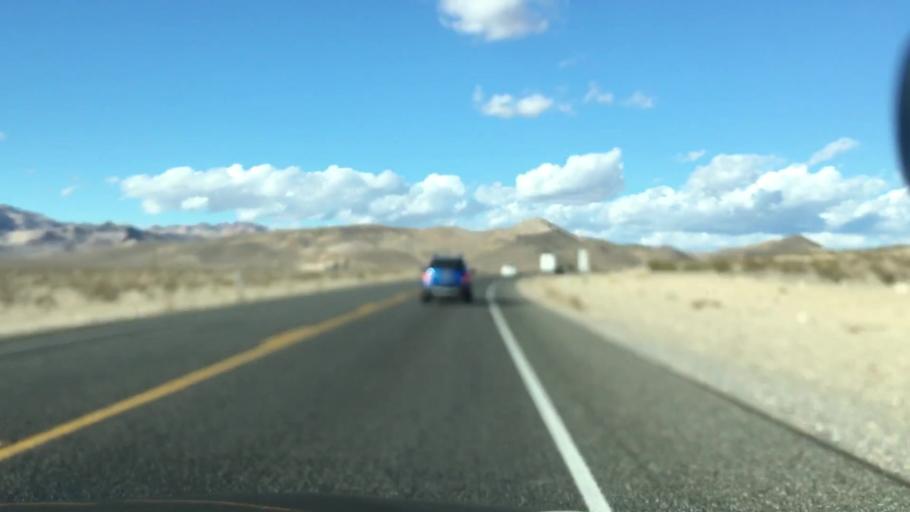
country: US
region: Nevada
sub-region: Nye County
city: Beatty
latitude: 36.8560
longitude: -116.7572
